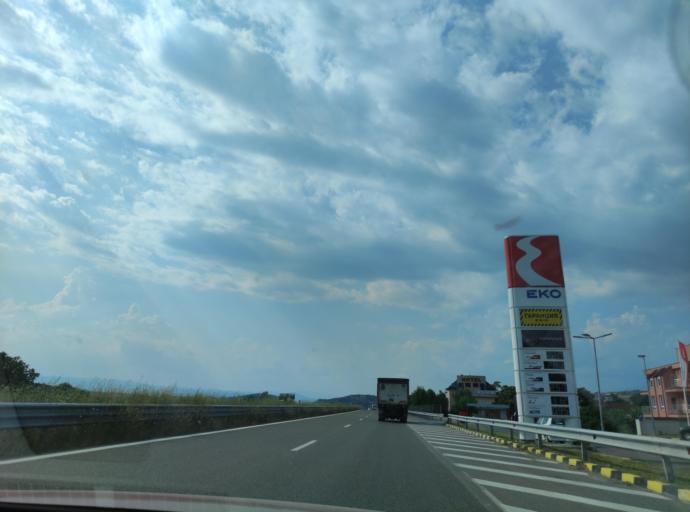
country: BG
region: Blagoevgrad
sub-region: Obshtina Petrich
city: Petrich
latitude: 41.3985
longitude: 23.3542
